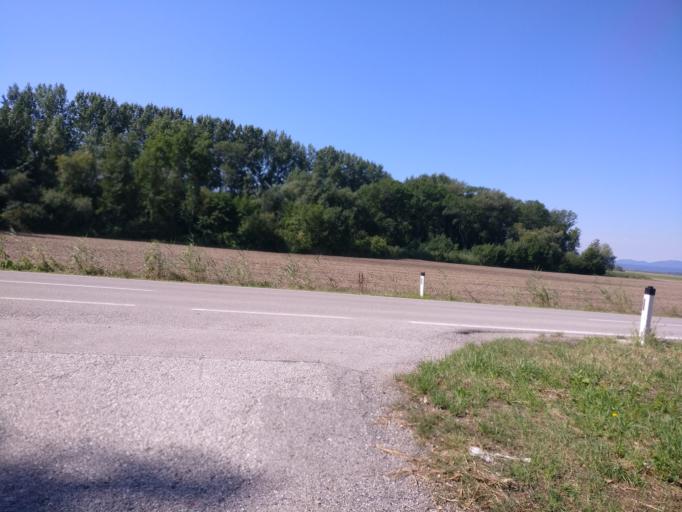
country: AT
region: Lower Austria
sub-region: Politischer Bezirk Baden
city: Pottendorf
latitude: 47.9240
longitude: 16.3666
